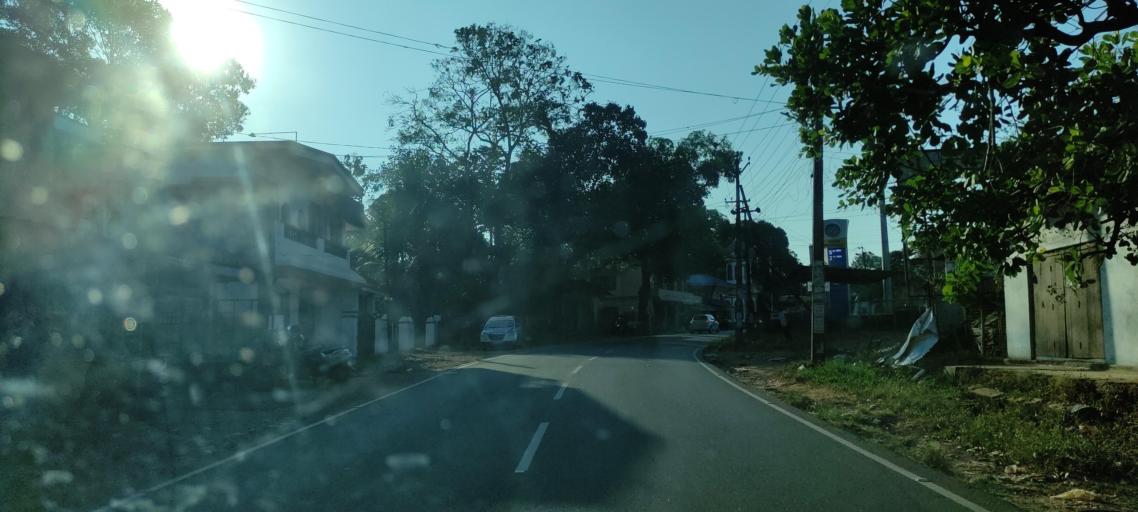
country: IN
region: Kerala
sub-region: Pattanamtitta
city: Adur
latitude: 9.1677
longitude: 76.6578
